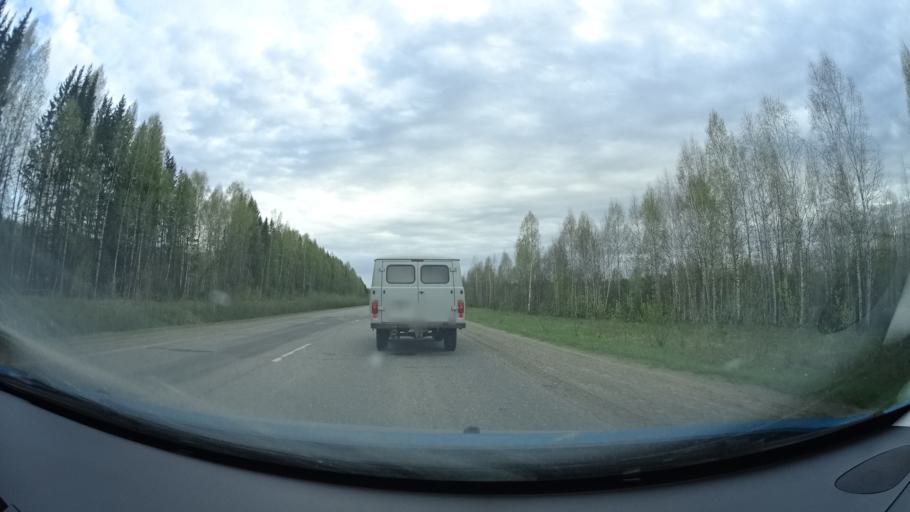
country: RU
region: Perm
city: Osa
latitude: 57.4428
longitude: 55.6378
